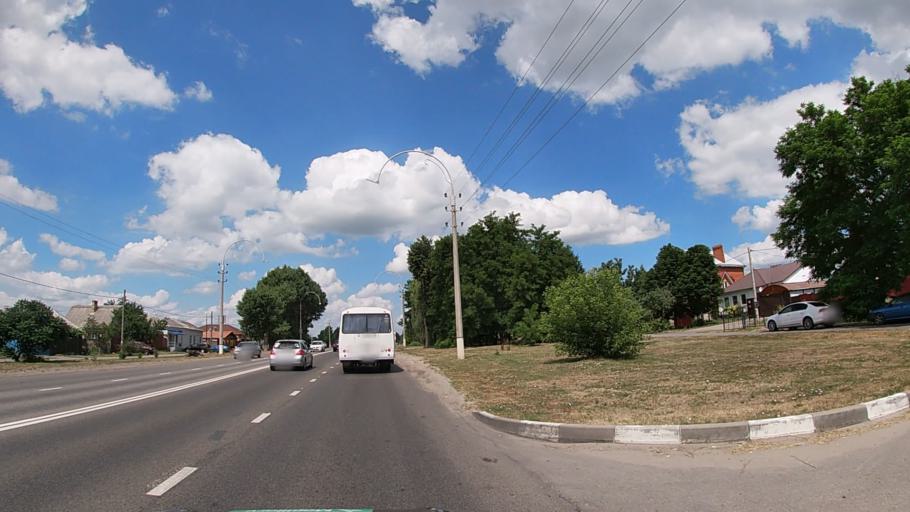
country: RU
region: Belgorod
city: Severnyy
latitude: 50.6259
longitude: 36.4974
